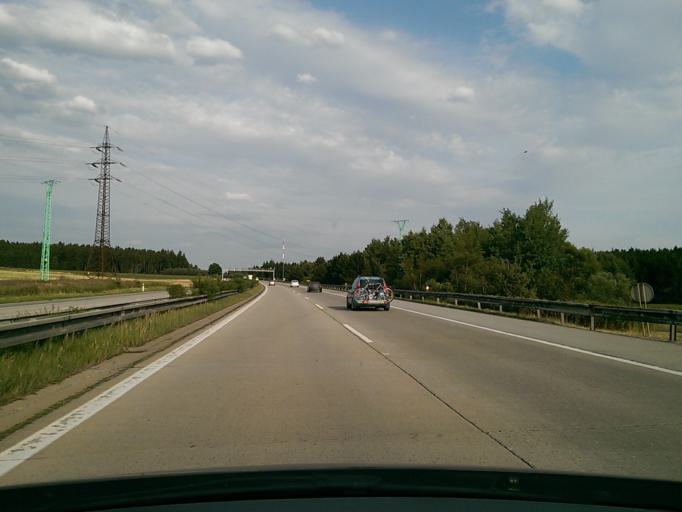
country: CZ
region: Vysocina
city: Velky Beranov
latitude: 49.4273
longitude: 15.6625
